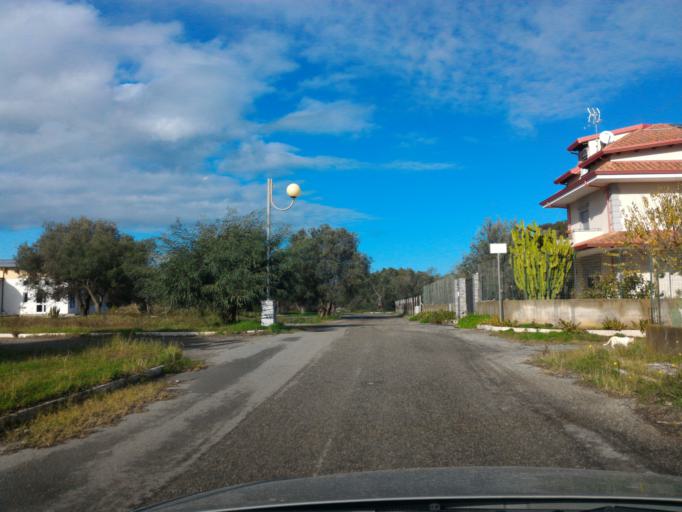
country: IT
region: Calabria
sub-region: Provincia di Crotone
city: Torretta
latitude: 39.4588
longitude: 17.0343
